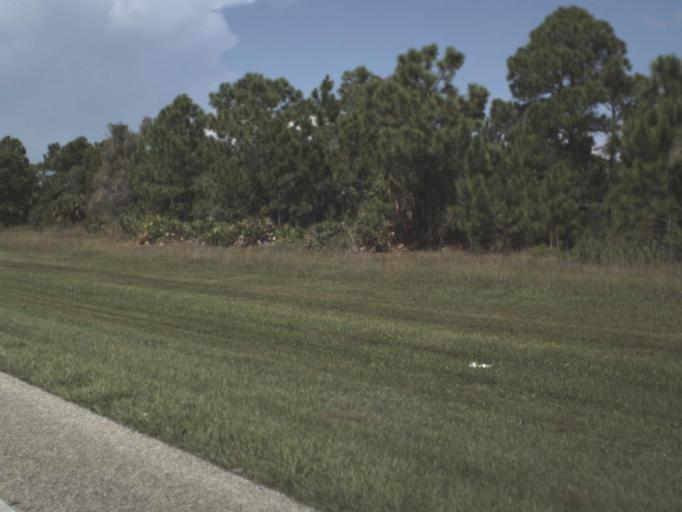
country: US
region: Florida
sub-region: Sarasota County
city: Plantation
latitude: 27.0498
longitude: -82.3737
